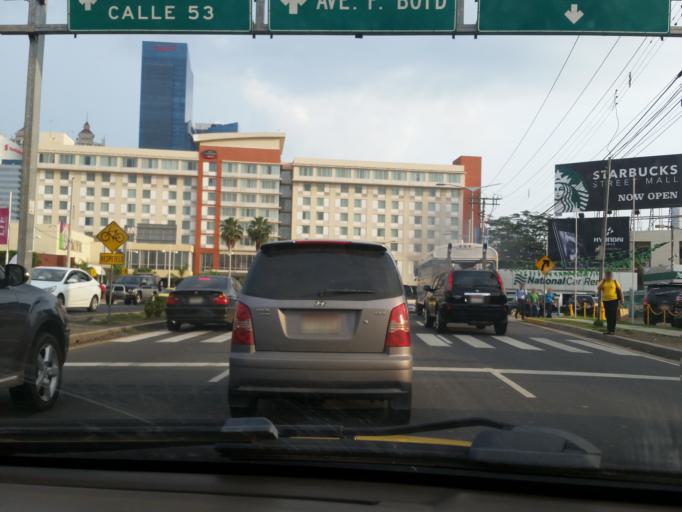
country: PA
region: Panama
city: Panama
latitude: 8.9861
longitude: -79.5124
